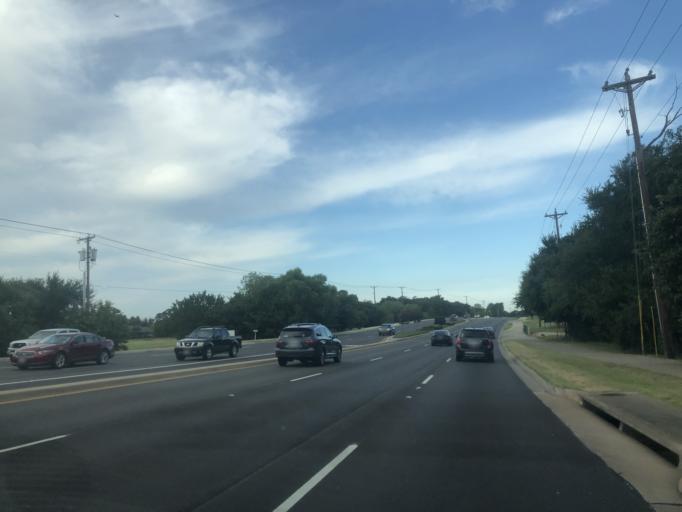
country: US
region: Texas
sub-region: Tarrant County
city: Keller
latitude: 32.9347
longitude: -97.1961
